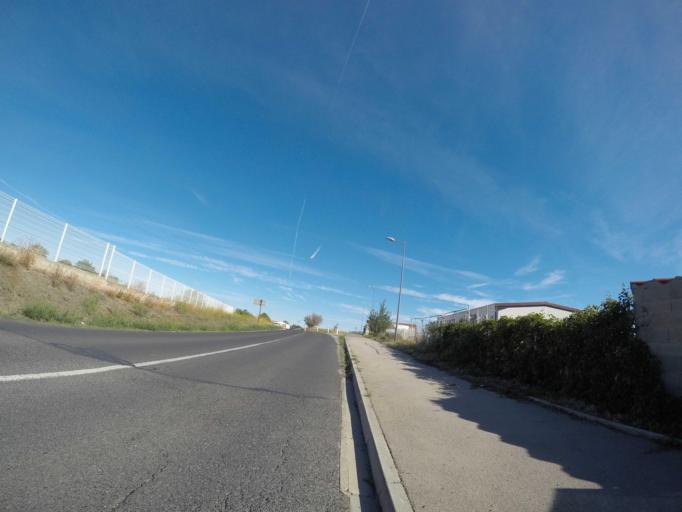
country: FR
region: Languedoc-Roussillon
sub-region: Departement des Pyrenees-Orientales
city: Trouillas
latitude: 42.6171
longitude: 2.8114
